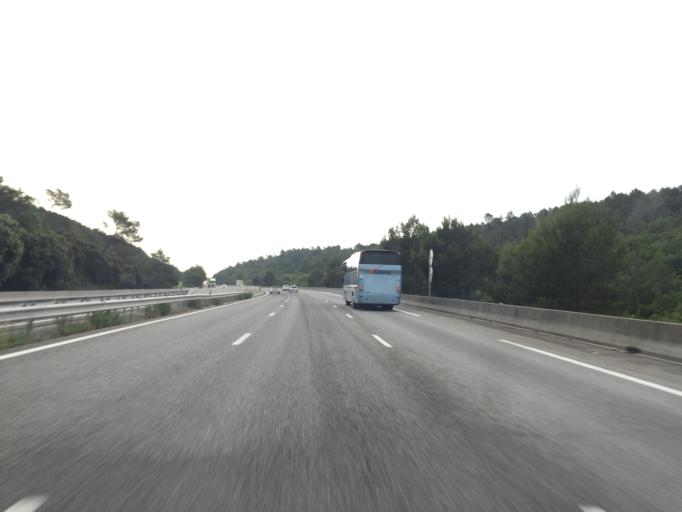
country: FR
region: Provence-Alpes-Cote d'Azur
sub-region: Departement du Var
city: Camps-la-Source
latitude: 43.4179
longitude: 6.1234
